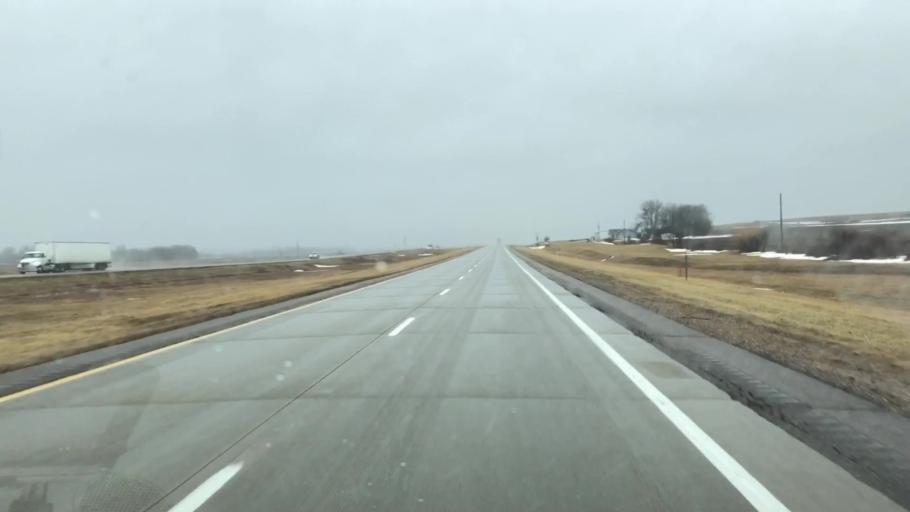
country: US
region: Iowa
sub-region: Sioux County
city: Orange City
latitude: 42.9026
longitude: -96.0849
